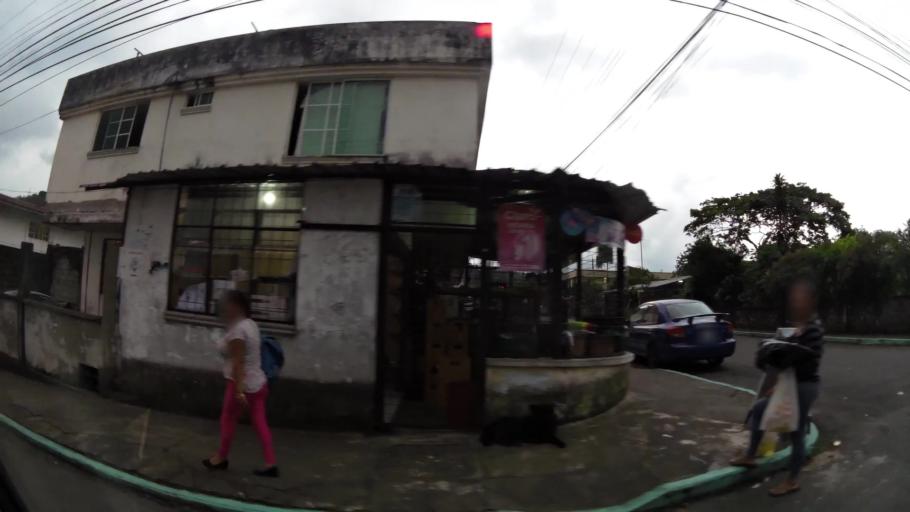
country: EC
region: Pastaza
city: Puyo
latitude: -1.4877
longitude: -78.0116
